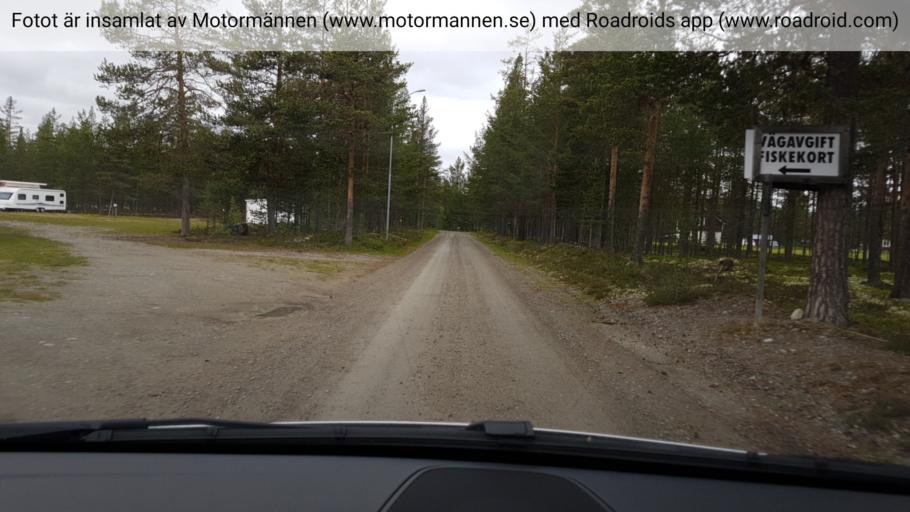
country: SE
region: Jaemtland
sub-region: Harjedalens Kommun
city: Sveg
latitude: 62.2400
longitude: 13.3392
